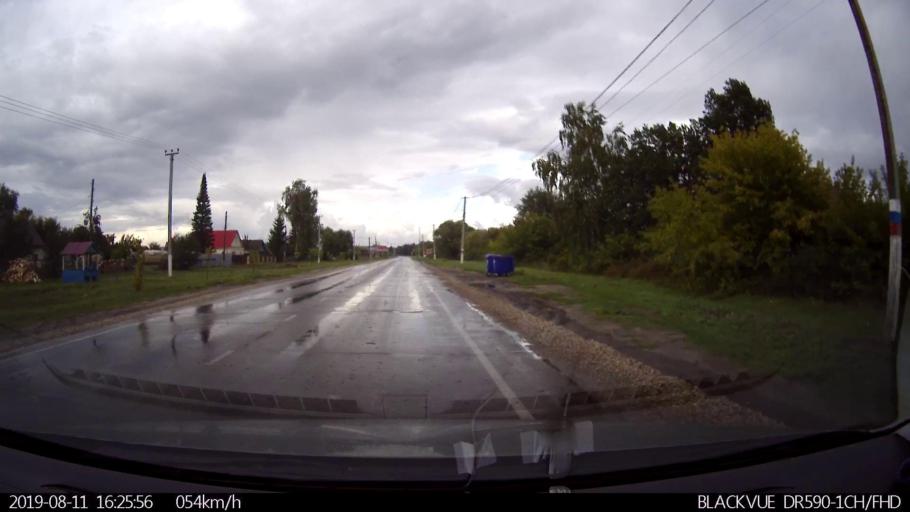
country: RU
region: Ulyanovsk
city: Mayna
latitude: 54.1080
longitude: 47.6106
